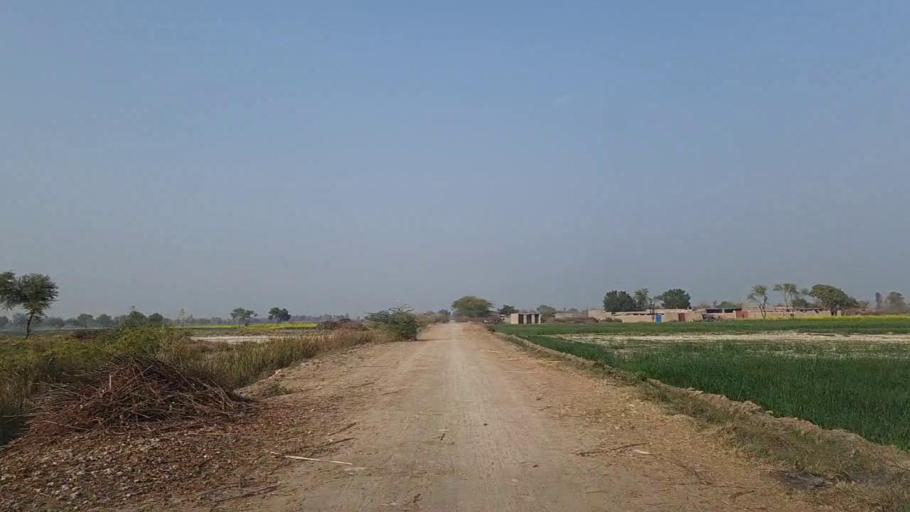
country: PK
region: Sindh
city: Nawabshah
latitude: 26.3482
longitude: 68.4740
